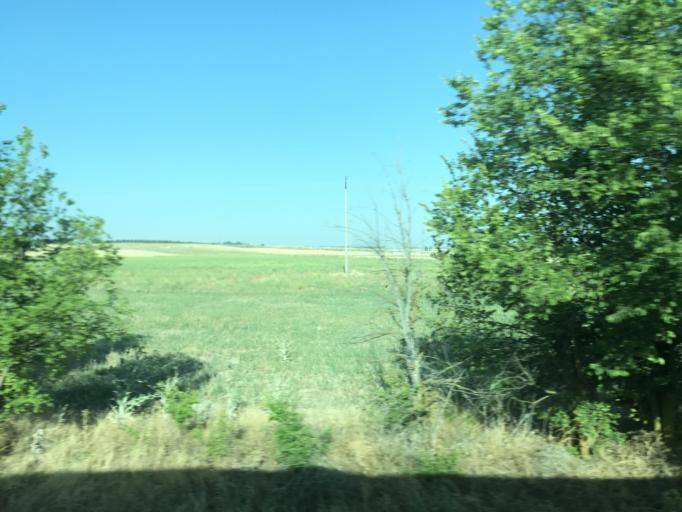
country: ES
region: Castille and Leon
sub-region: Provincia de Valladolid
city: Olmedo
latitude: 41.2959
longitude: -4.6819
